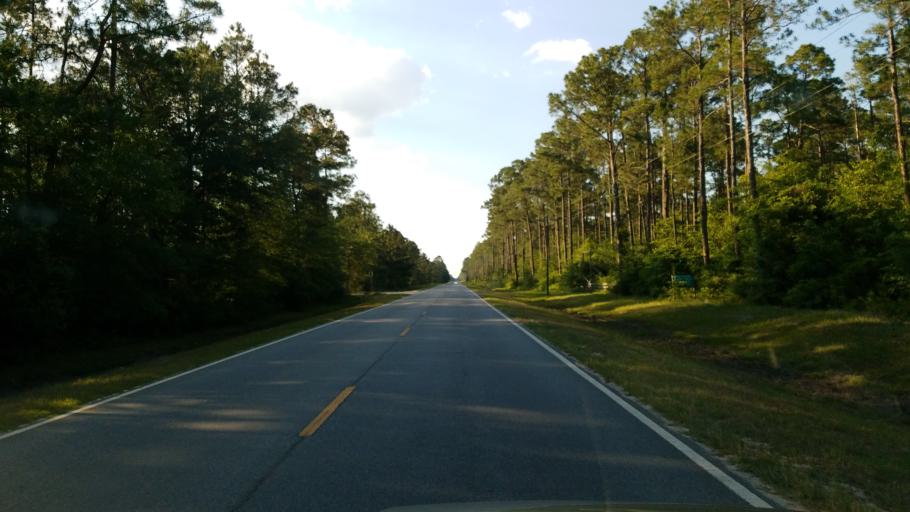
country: US
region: Georgia
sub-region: Lanier County
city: Lakeland
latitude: 31.0859
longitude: -83.0763
